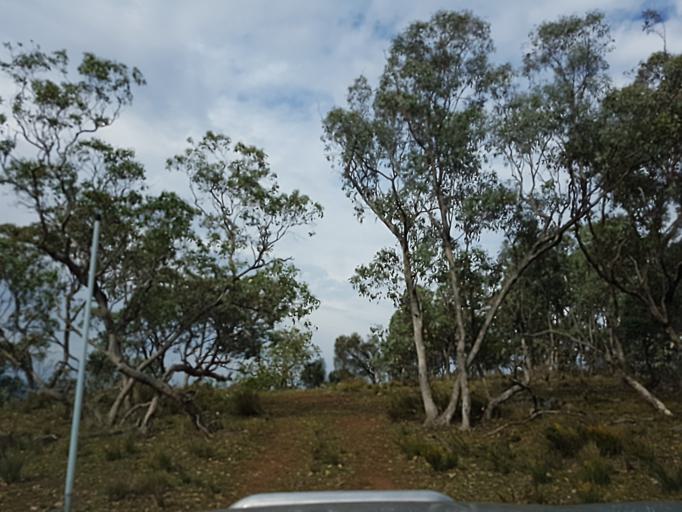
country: AU
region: New South Wales
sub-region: Snowy River
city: Jindabyne
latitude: -36.9694
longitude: 148.3933
